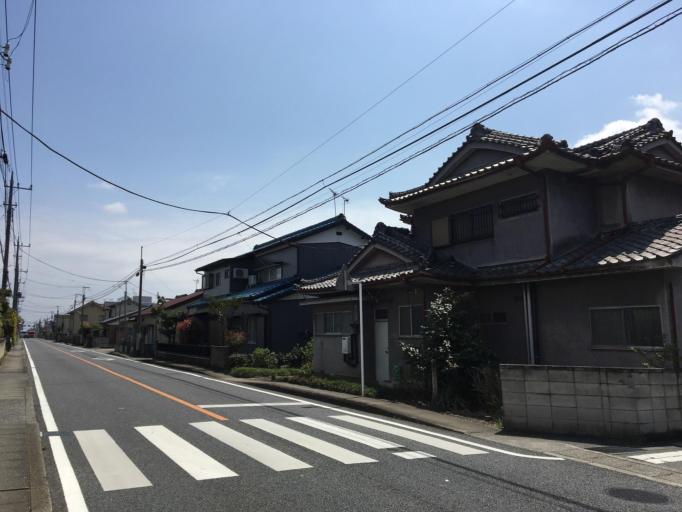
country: JP
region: Gunma
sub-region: Sawa-gun
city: Tamamura
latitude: 36.3033
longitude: 139.1034
